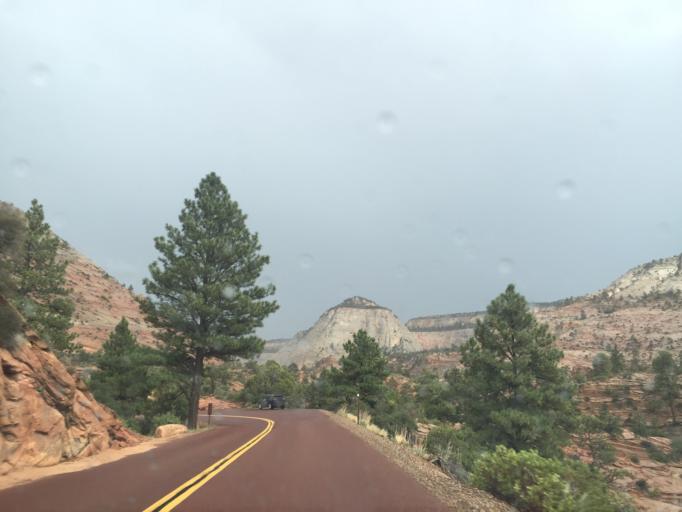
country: US
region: Utah
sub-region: Washington County
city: Hildale
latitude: 37.2236
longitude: -112.9125
